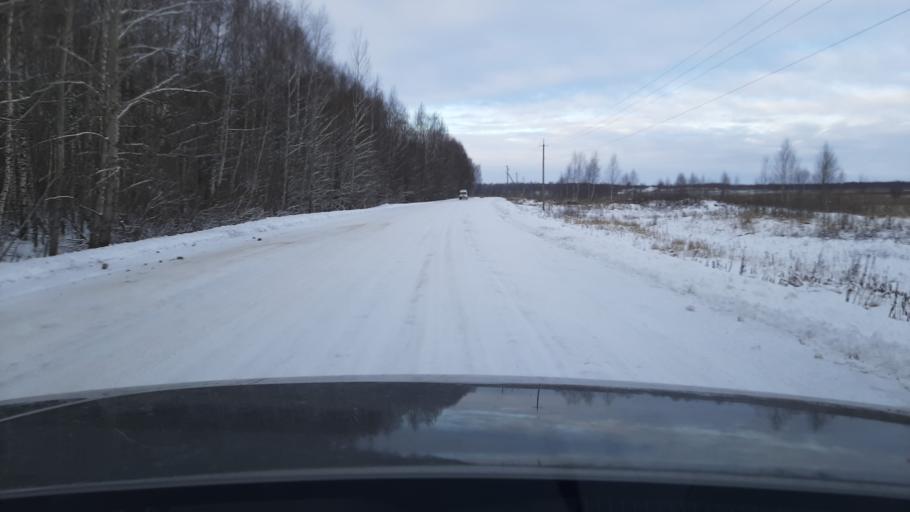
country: RU
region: Kostroma
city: Nerekhta
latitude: 57.4709
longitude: 40.6763
